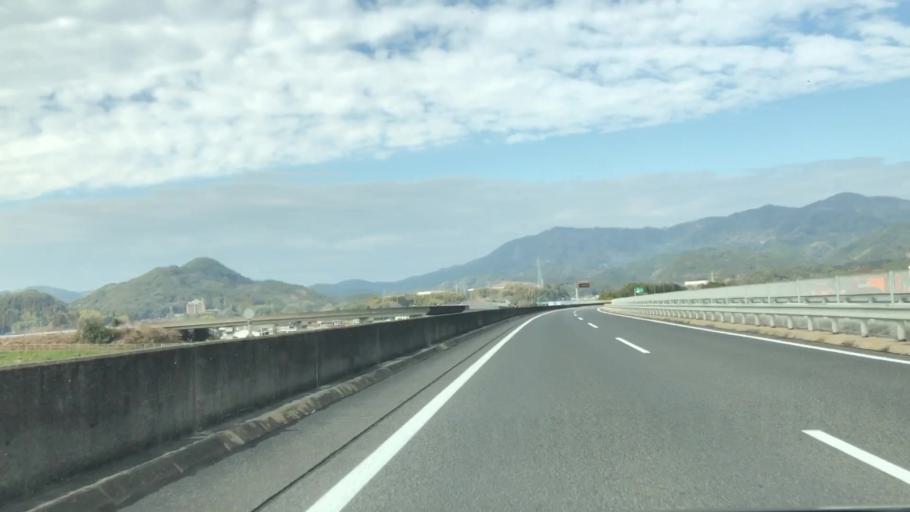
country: JP
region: Saga Prefecture
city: Takeocho-takeo
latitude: 33.2123
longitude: 130.0528
